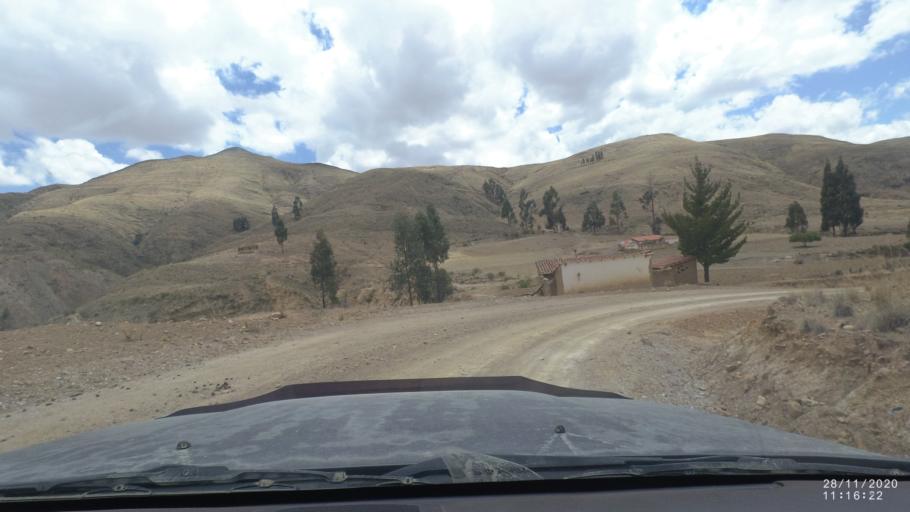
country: BO
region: Cochabamba
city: Tarata
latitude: -17.7465
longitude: -66.0842
